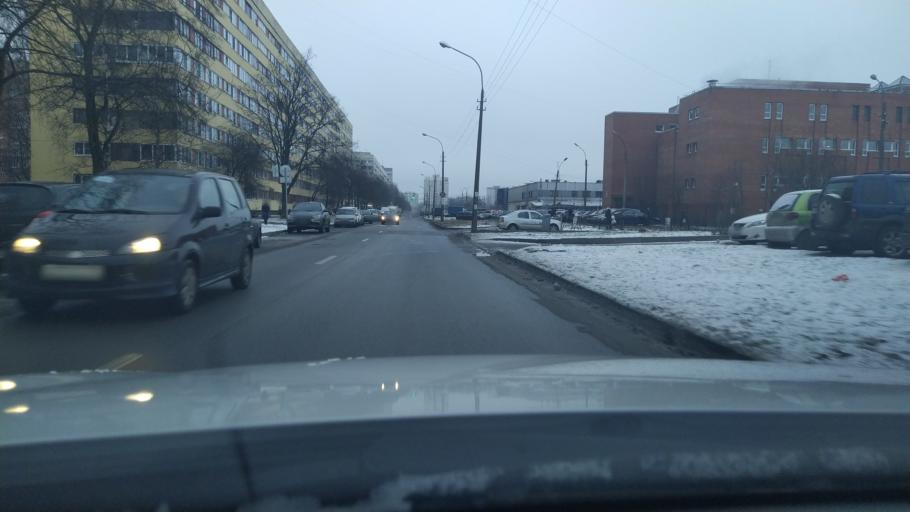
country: RU
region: St.-Petersburg
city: Grazhdanka
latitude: 60.0435
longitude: 30.3933
